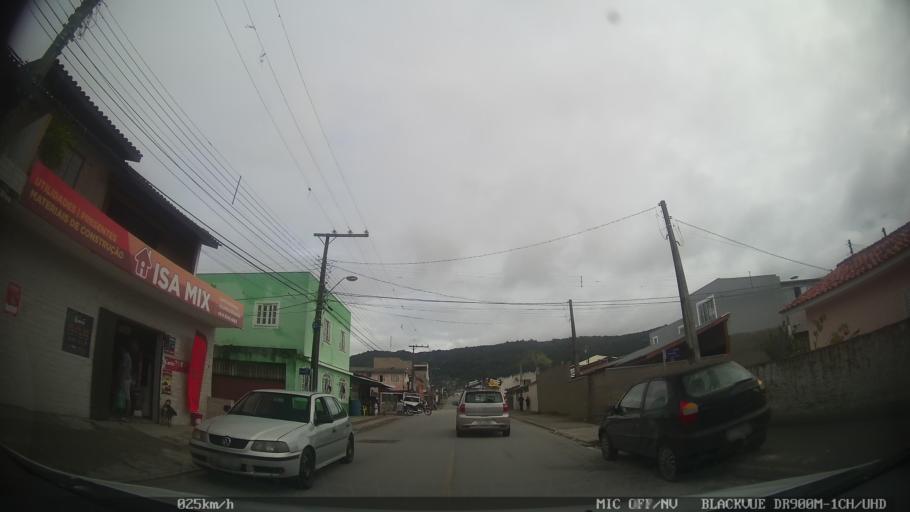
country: BR
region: Santa Catarina
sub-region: Biguacu
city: Biguacu
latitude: -27.5391
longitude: -48.6417
